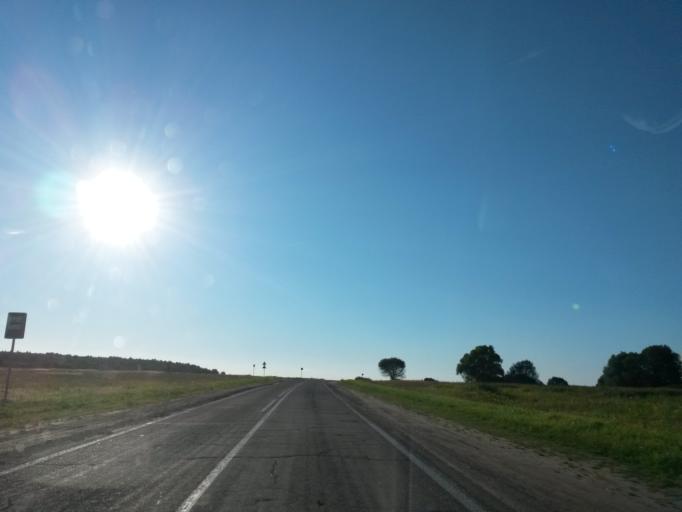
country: RU
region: Jaroslavl
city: Gavrilov-Yam
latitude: 57.2824
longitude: 39.9029
